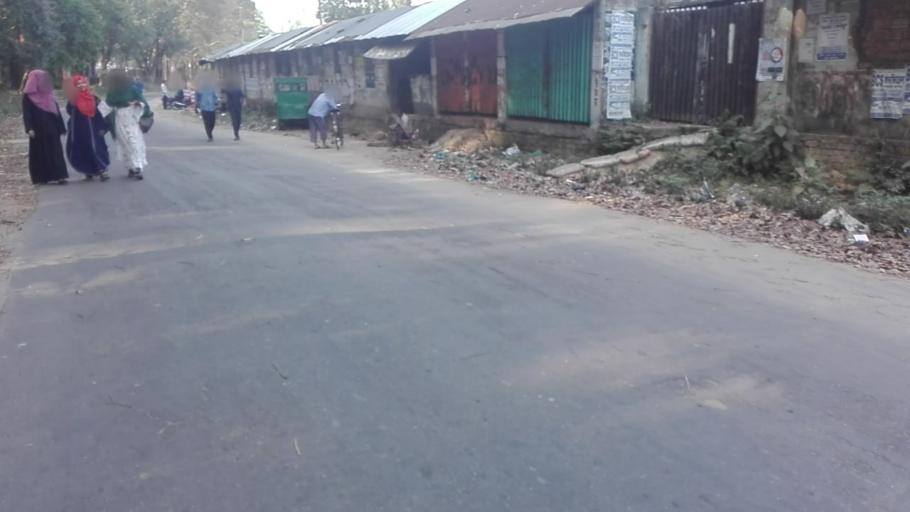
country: BD
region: Chittagong
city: Chittagong
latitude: 22.4715
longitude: 91.7934
